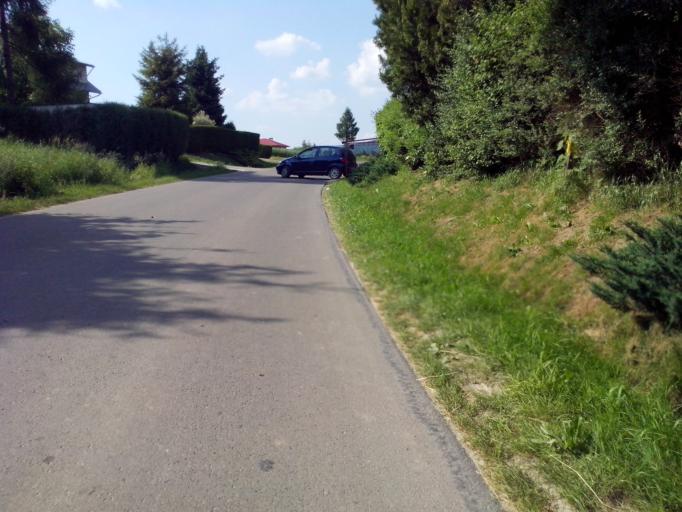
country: PL
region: Subcarpathian Voivodeship
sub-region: Powiat brzozowski
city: Blizne
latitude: 49.7442
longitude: 21.9740
